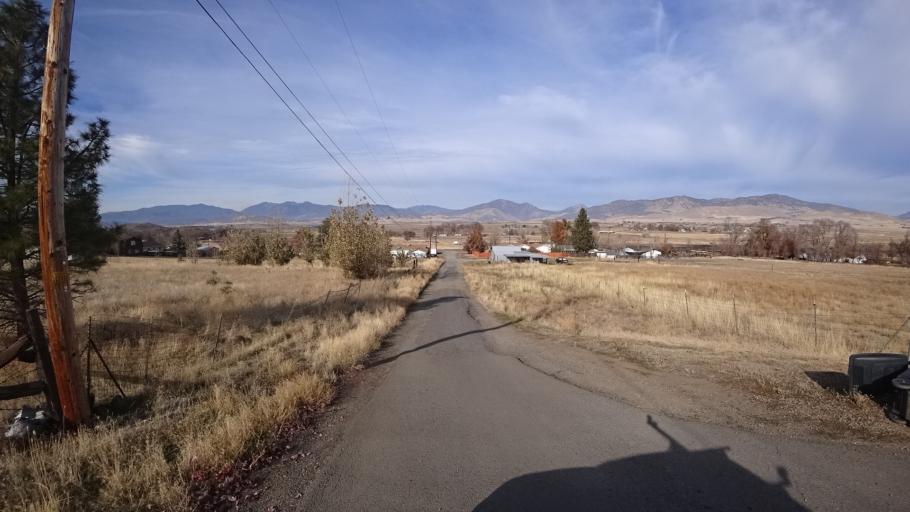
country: US
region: California
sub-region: Siskiyou County
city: Montague
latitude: 41.7332
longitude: -122.5176
